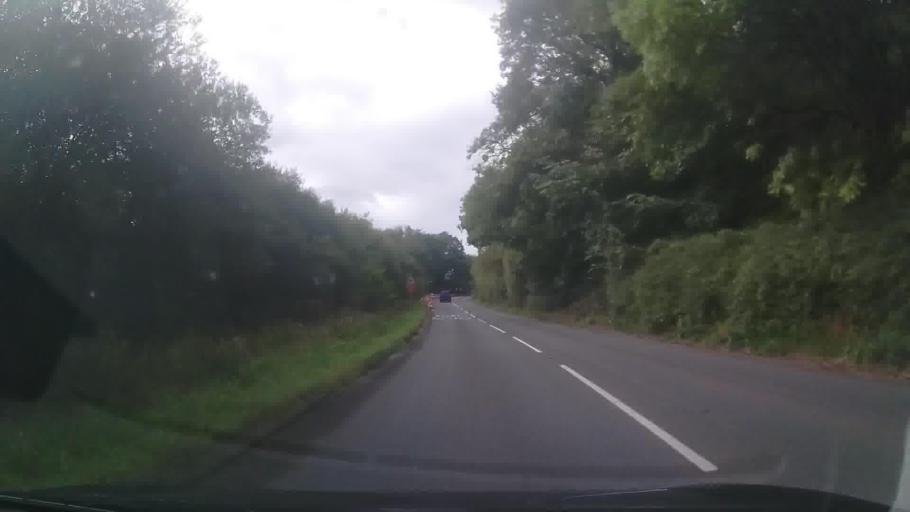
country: GB
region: Wales
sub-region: Gwynedd
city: Dolgellau
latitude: 52.7578
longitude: -3.9183
